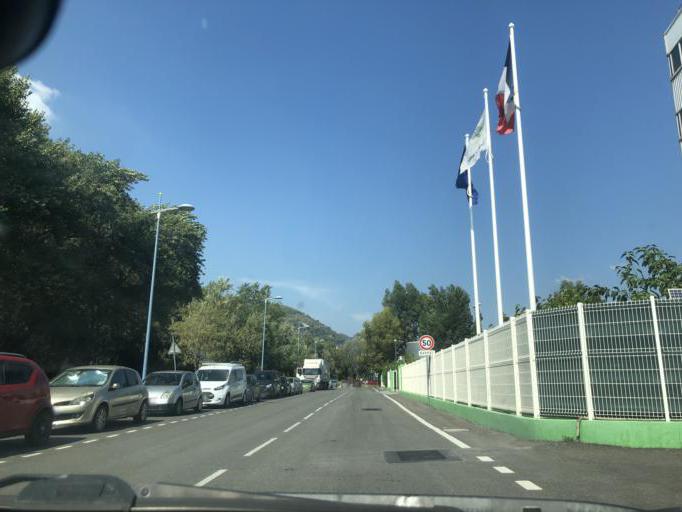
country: FR
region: Provence-Alpes-Cote d'Azur
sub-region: Departement des Alpes-Maritimes
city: Carros
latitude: 43.7877
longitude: 7.2084
